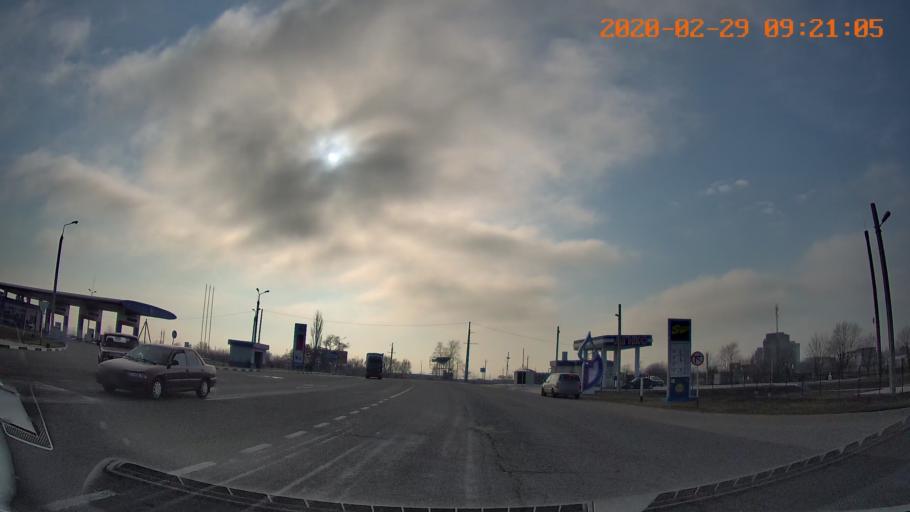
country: MD
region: Telenesti
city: Pervomaisc
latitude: 46.7406
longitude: 29.9548
